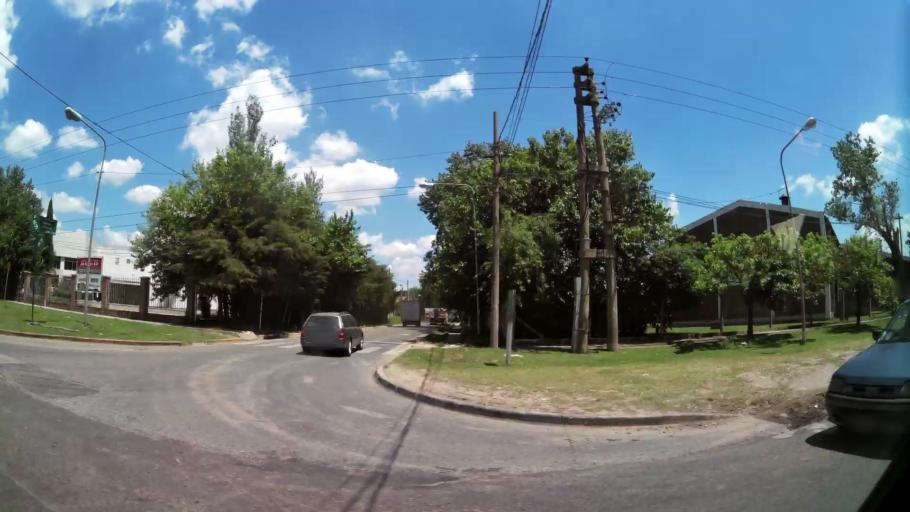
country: AR
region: Buenos Aires
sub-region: Partido de Tigre
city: Tigre
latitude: -34.4430
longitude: -58.5972
